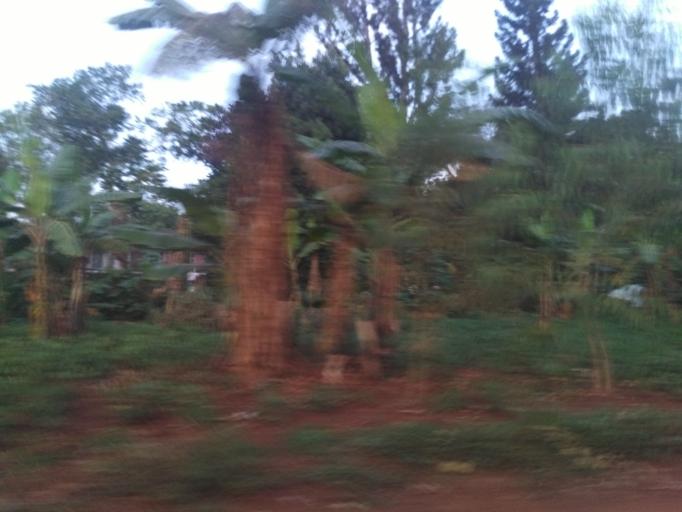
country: UG
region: Eastern Region
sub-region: Jinja District
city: Jinja
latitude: 0.4312
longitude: 33.1972
